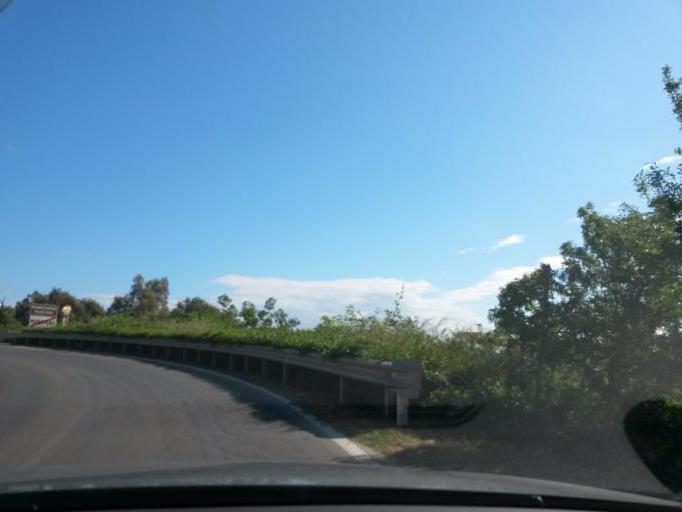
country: IT
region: Tuscany
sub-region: Provincia di Livorno
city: Marciana Marina
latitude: 42.7889
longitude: 10.2270
